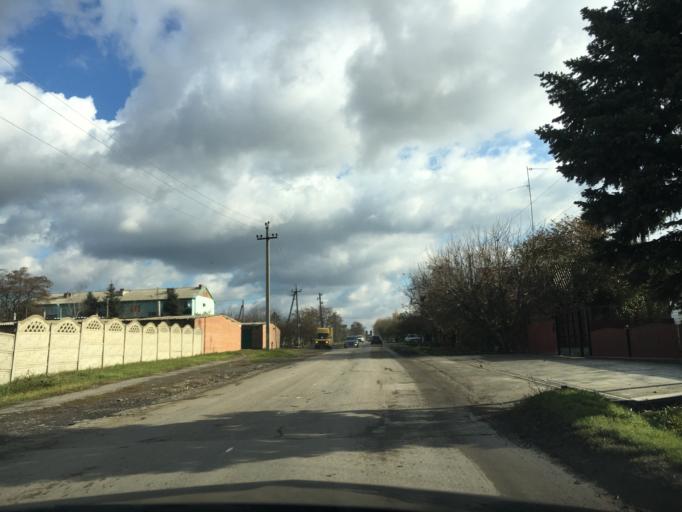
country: RU
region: Rostov
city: Matveyev Kurgan
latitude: 47.5634
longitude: 38.8773
